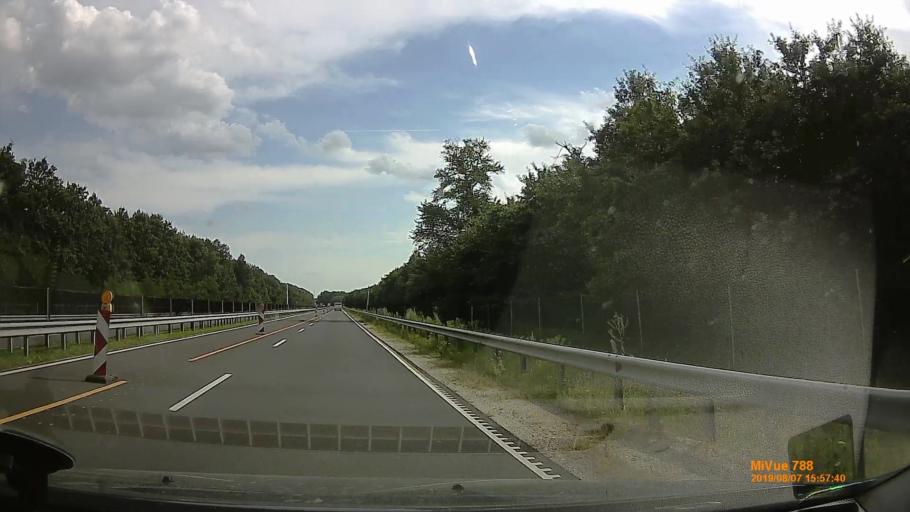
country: HU
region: Vas
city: Kormend
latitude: 47.0379
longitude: 16.6132
